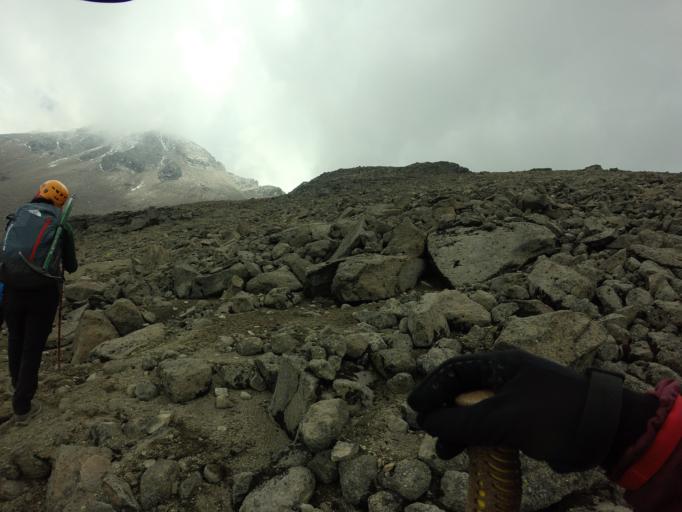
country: MX
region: Mexico
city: Amecameca de Juarez
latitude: 19.1534
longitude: -98.6409
